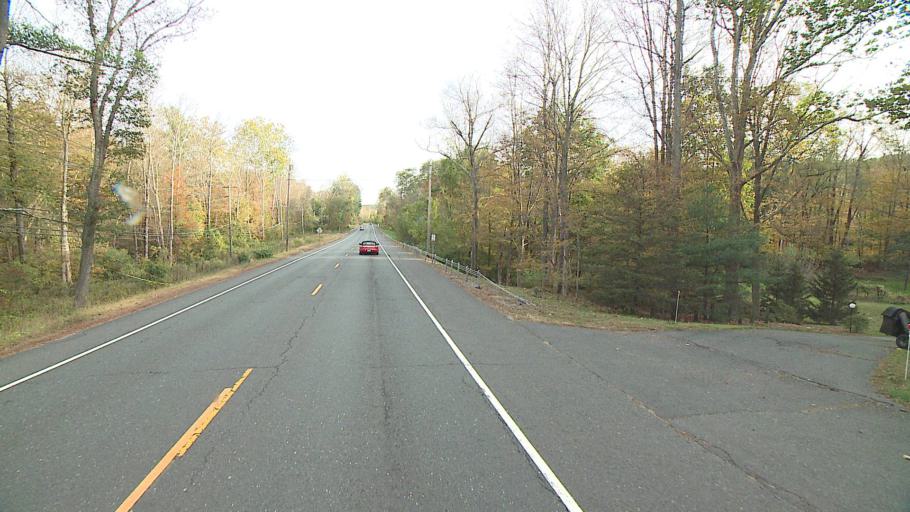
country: US
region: Connecticut
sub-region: Hartford County
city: Collinsville
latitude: 41.8444
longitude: -72.9412
